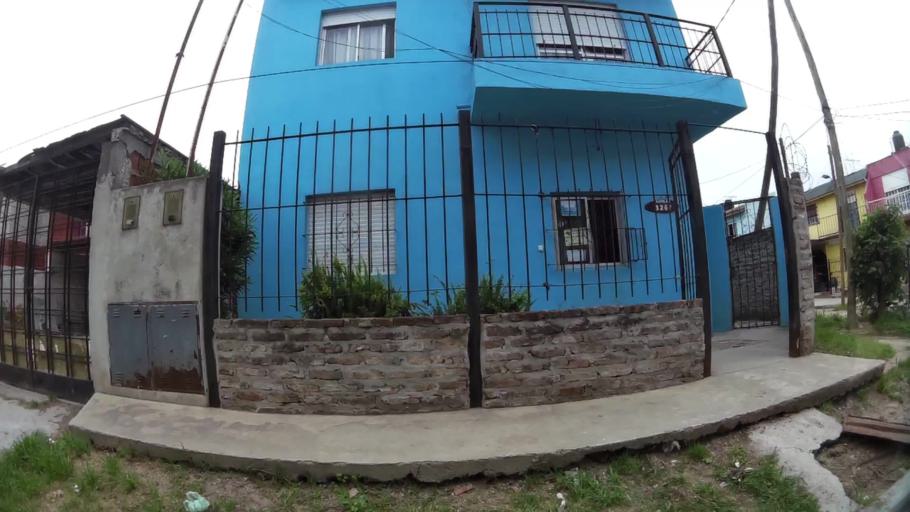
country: AR
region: Buenos Aires
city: San Justo
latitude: -34.6986
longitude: -58.5458
